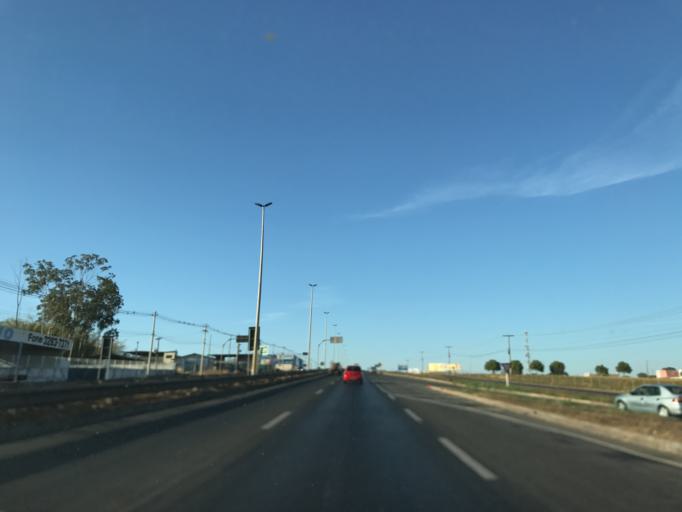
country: BR
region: Goias
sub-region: Aparecida De Goiania
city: Aparecida de Goiania
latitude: -16.7941
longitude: -49.2383
